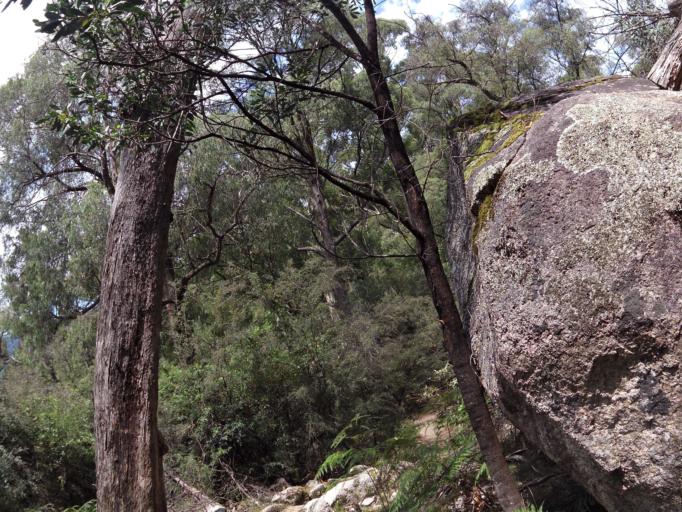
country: AU
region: Victoria
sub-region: Alpine
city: Mount Beauty
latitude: -36.7164
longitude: 146.8403
